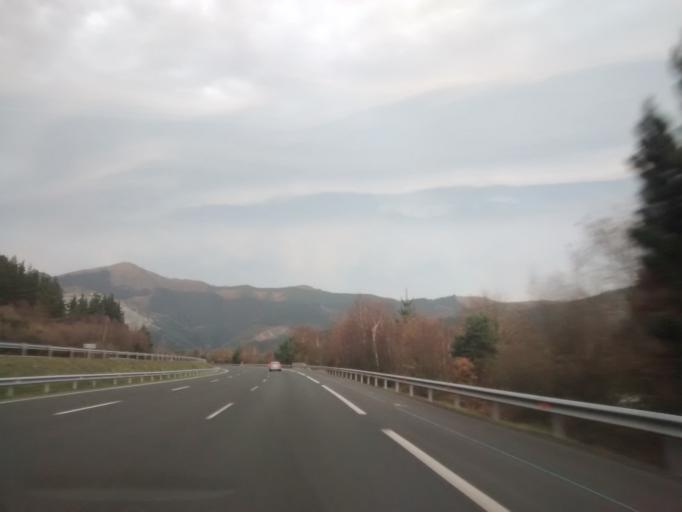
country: ES
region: Basque Country
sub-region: Bizkaia
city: Elexalde
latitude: 43.1004
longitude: -2.9167
